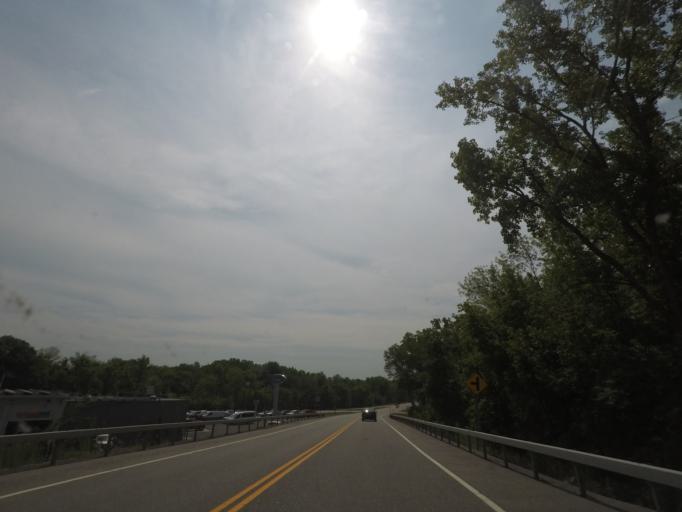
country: US
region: New York
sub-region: Saratoga County
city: Mechanicville
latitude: 42.8836
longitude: -73.6870
